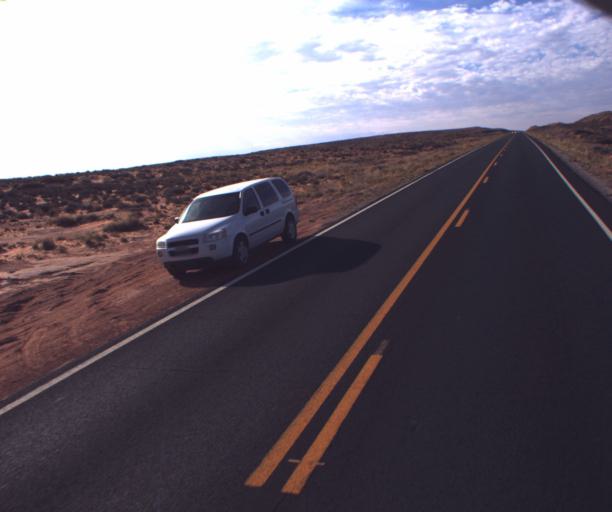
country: US
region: Arizona
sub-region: Apache County
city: Many Farms
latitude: 36.8948
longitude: -109.6263
